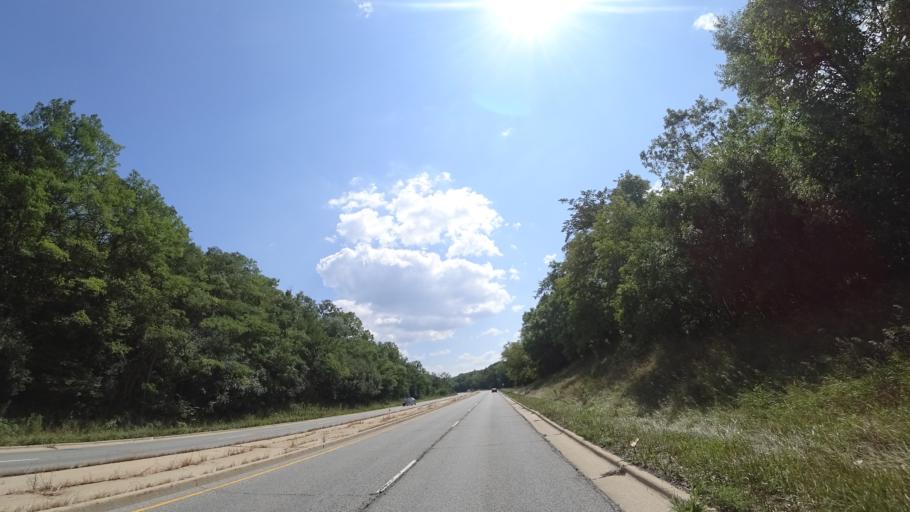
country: US
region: Illinois
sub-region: Cook County
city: Palos Heights
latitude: 41.6280
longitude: -87.7957
